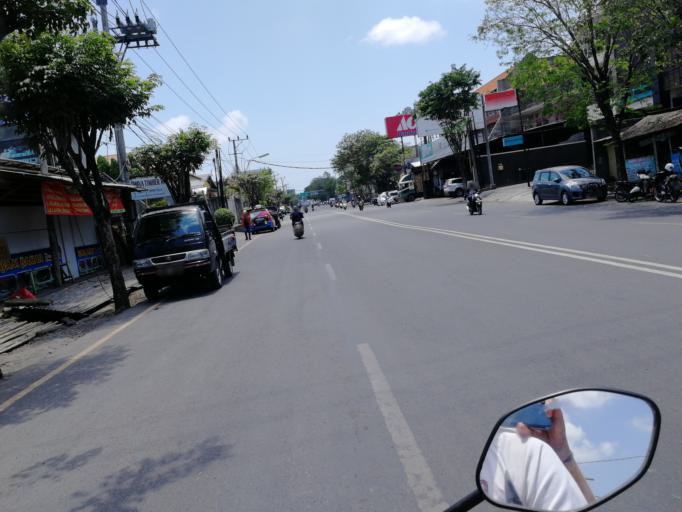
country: ID
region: Bali
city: Banjar Kertasari
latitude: -8.6370
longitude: 115.1789
